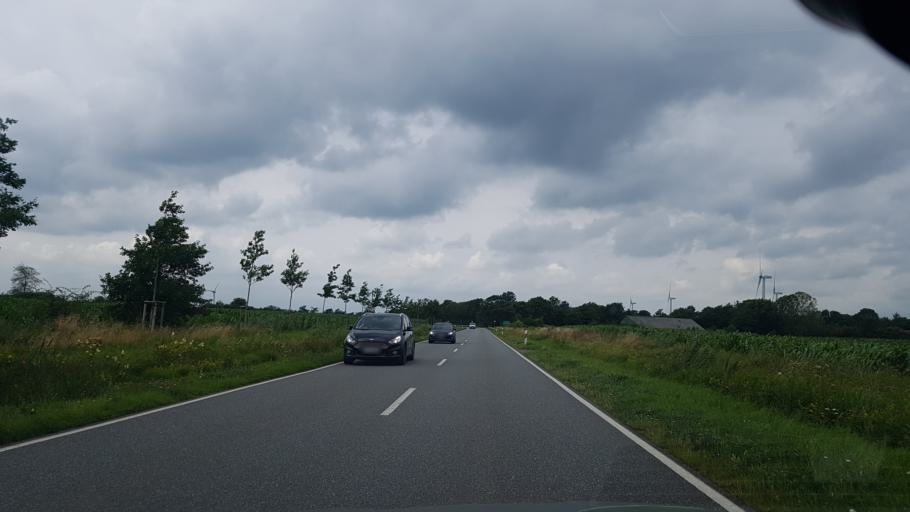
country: DE
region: Schleswig-Holstein
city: Boxlund
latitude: 54.8549
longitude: 9.1792
